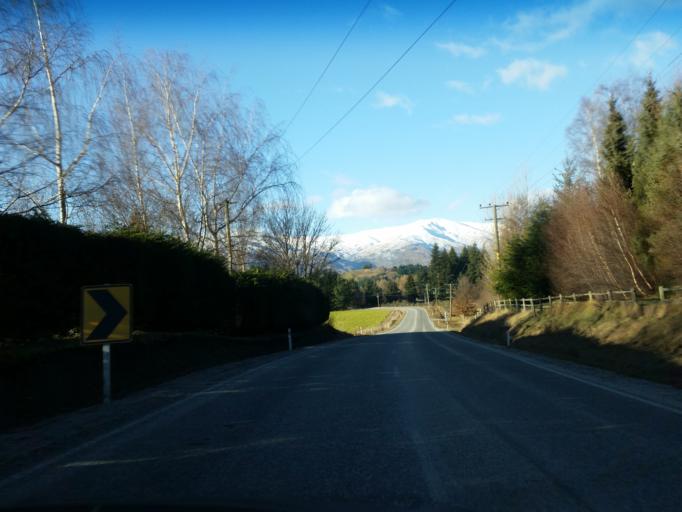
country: NZ
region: Otago
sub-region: Queenstown-Lakes District
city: Arrowtown
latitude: -44.9560
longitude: 168.7368
